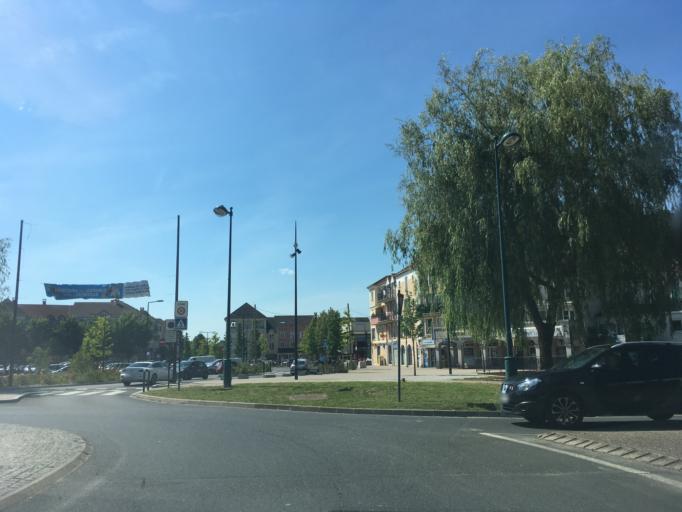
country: FR
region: Ile-de-France
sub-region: Departement de Seine-et-Marne
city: Bailly-Romainvilliers
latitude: 48.8511
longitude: 2.8190
